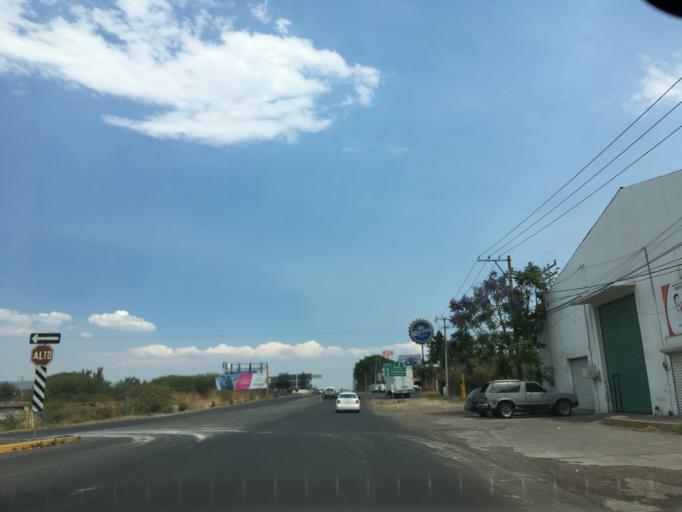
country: MX
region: Guanajuato
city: Moroleon
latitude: 20.1021
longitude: -101.1633
